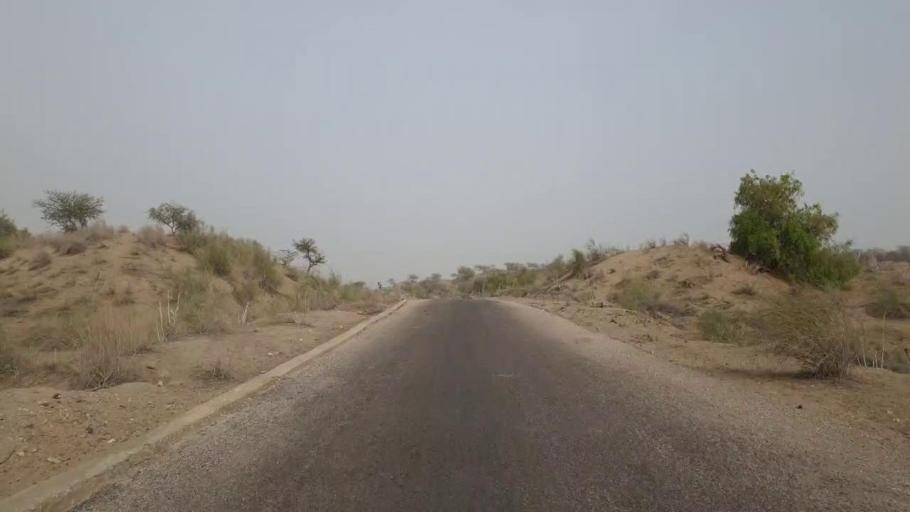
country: PK
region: Sindh
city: Islamkot
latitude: 24.5881
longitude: 70.2917
